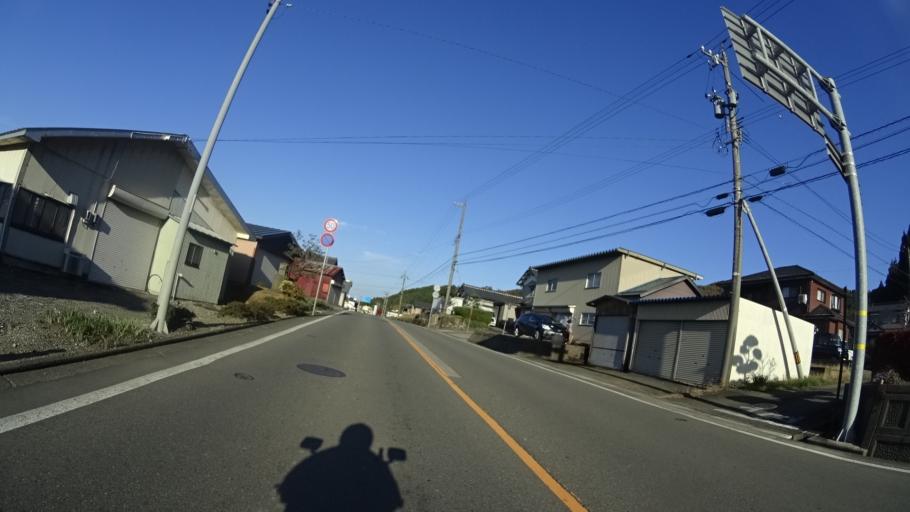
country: JP
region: Fukui
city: Maruoka
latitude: 36.1053
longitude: 136.3278
